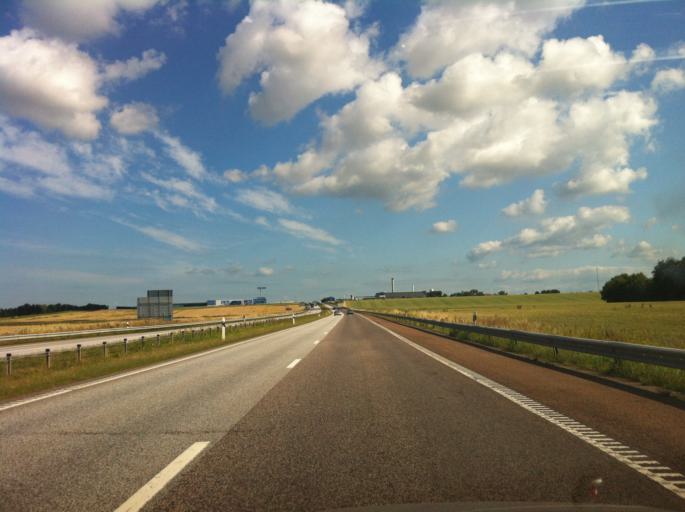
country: SE
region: Skane
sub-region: Angelholms Kommun
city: AEngelholm
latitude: 56.2344
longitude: 12.8987
